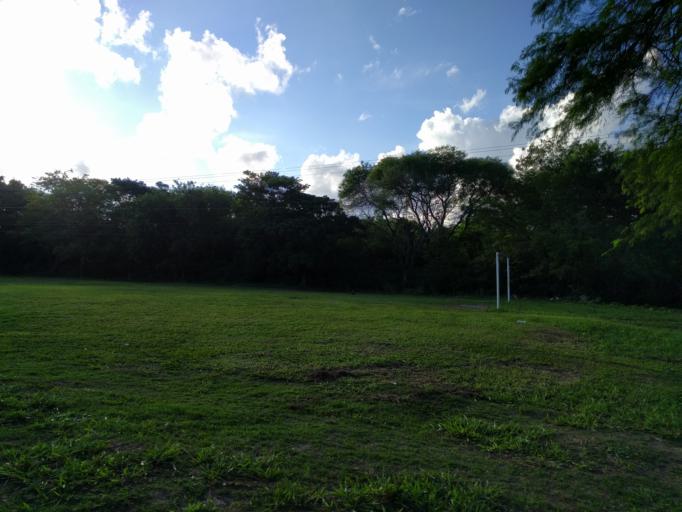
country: BO
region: Santa Cruz
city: Santa Cruz de la Sierra
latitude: -17.7712
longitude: -63.2109
